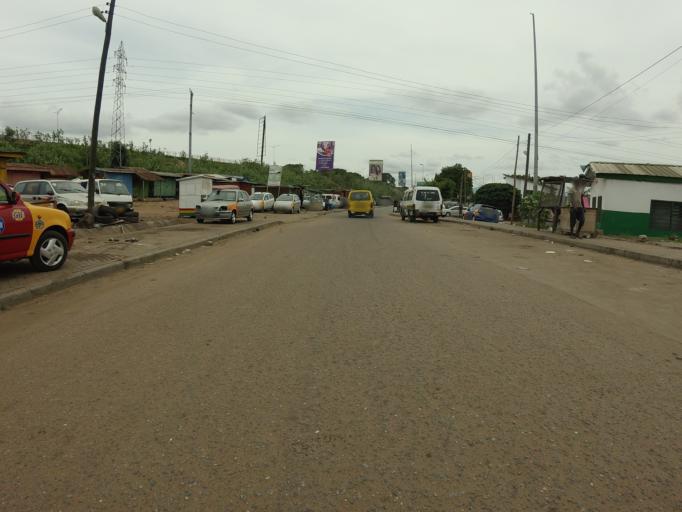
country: GH
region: Greater Accra
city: Accra
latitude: 5.5909
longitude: -0.2186
